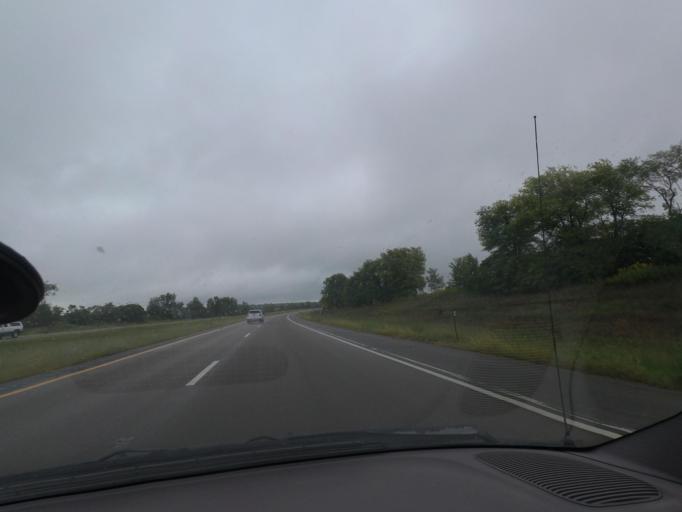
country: US
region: Illinois
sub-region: Piatt County
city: Monticello
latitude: 40.1096
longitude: -88.4877
